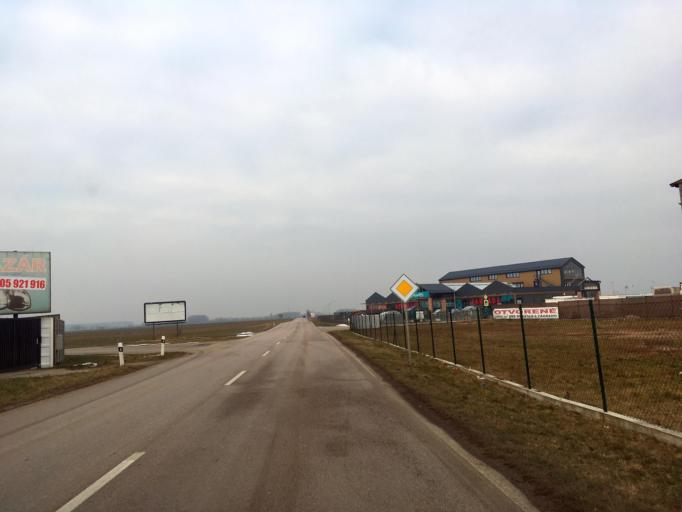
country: SK
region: Nitriansky
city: Sellye
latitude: 48.1766
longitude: 17.8612
